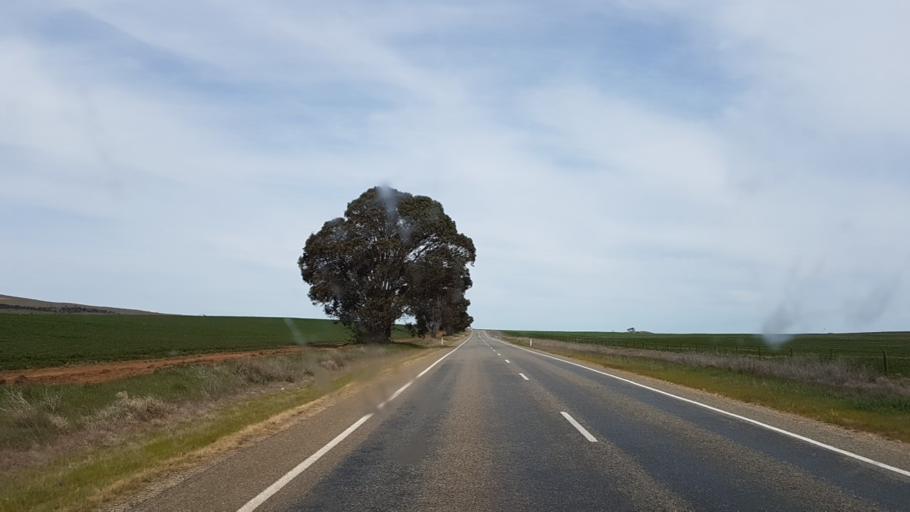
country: AU
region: South Australia
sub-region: Northern Areas
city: Jamestown
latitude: -33.0959
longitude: 138.6196
